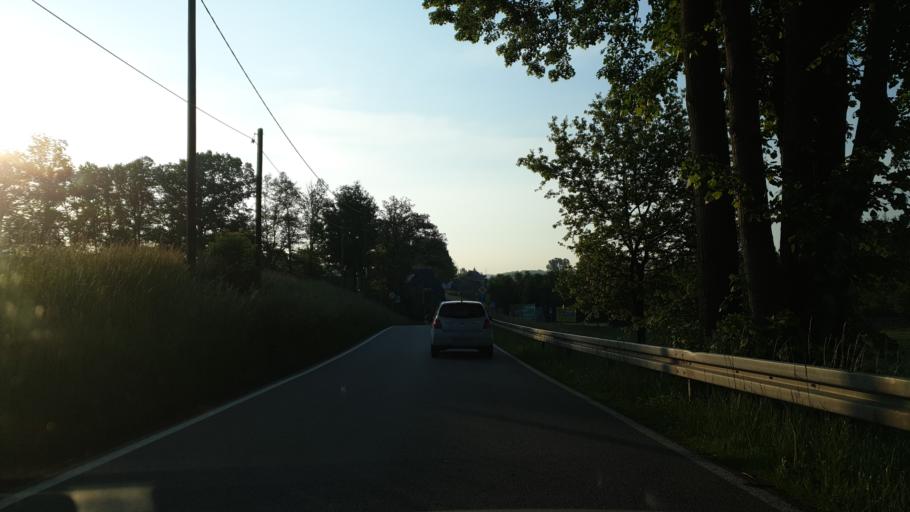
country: DE
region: Saxony
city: Bernsdorf
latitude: 50.7855
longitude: 12.6623
